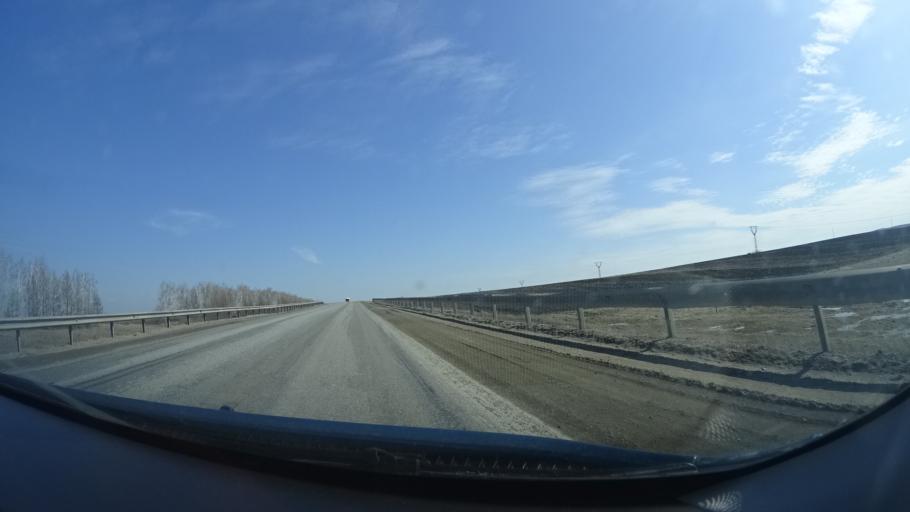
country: RU
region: Bashkortostan
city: Serafimovskiy
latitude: 54.4561
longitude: 53.6858
